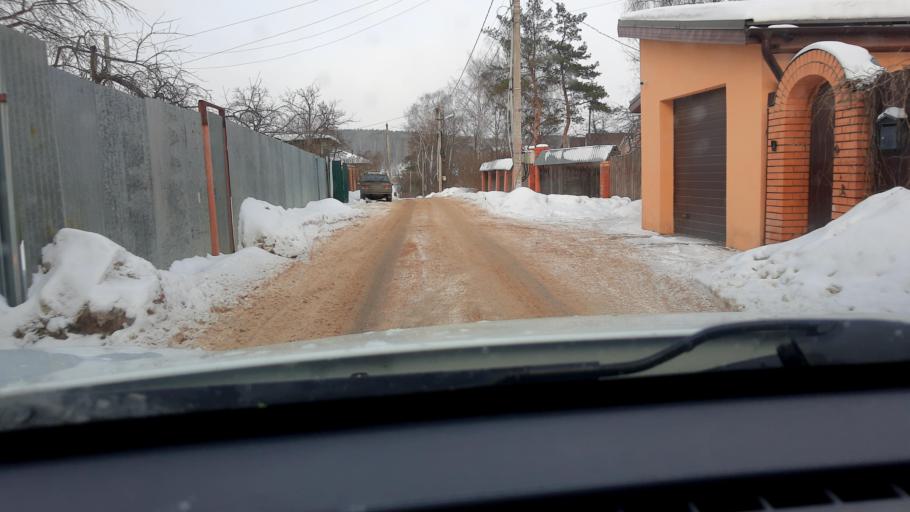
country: RU
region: Moskovskaya
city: Pavlovskaya Sloboda
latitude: 55.8209
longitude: 37.0934
